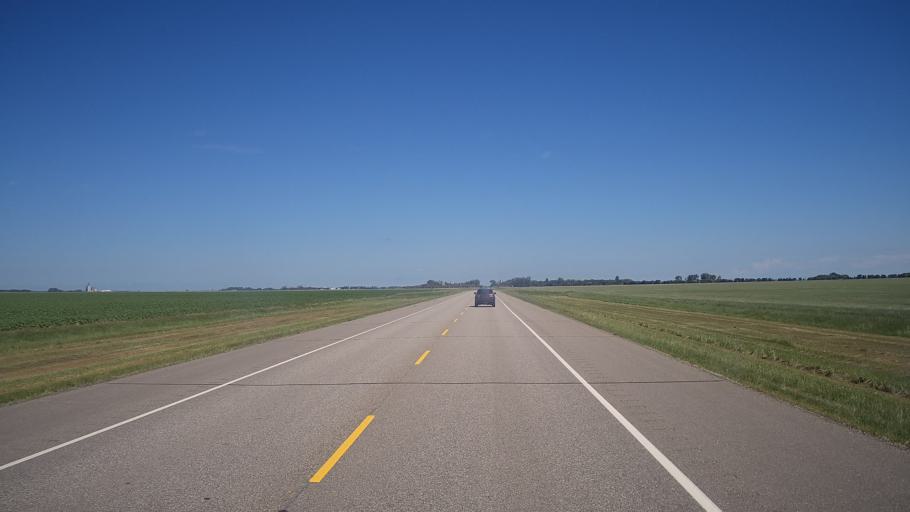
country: CA
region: Manitoba
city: Portage la Prairie
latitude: 50.0385
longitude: -98.4690
